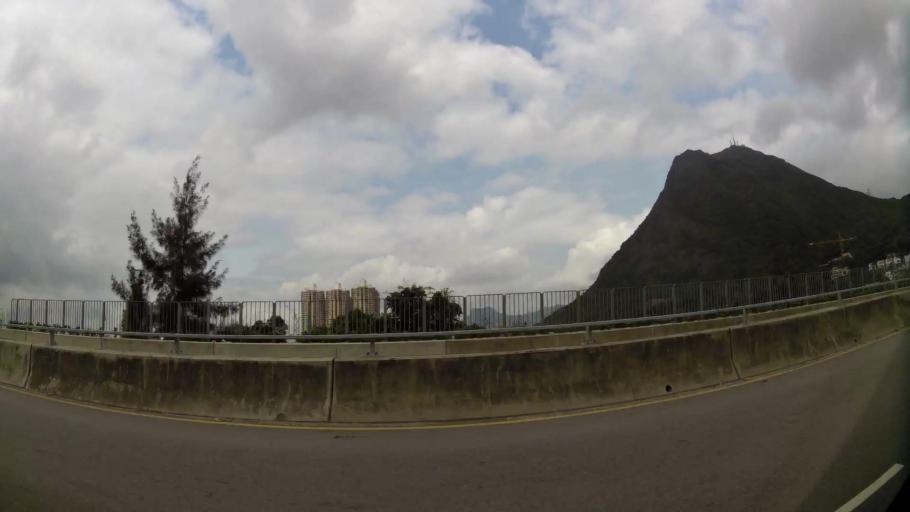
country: HK
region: Kowloon City
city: Kowloon
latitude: 22.3310
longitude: 114.2282
